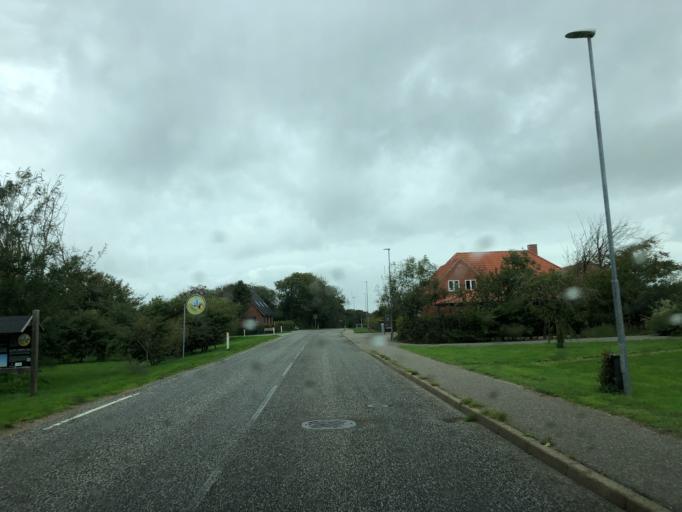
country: DK
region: North Denmark
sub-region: Thisted Kommune
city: Hurup
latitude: 56.7214
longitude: 8.3543
